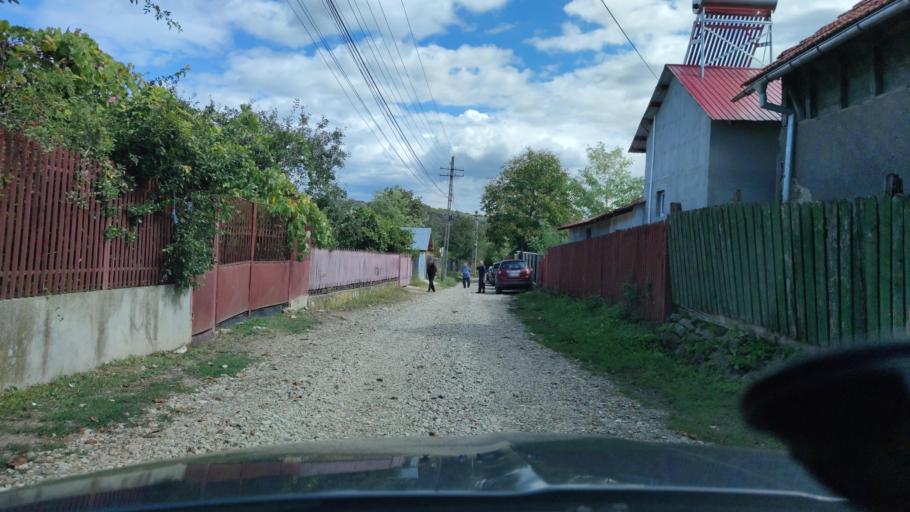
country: RO
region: Buzau
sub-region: Comuna Beceni
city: Valea Parului
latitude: 45.3621
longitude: 26.7634
